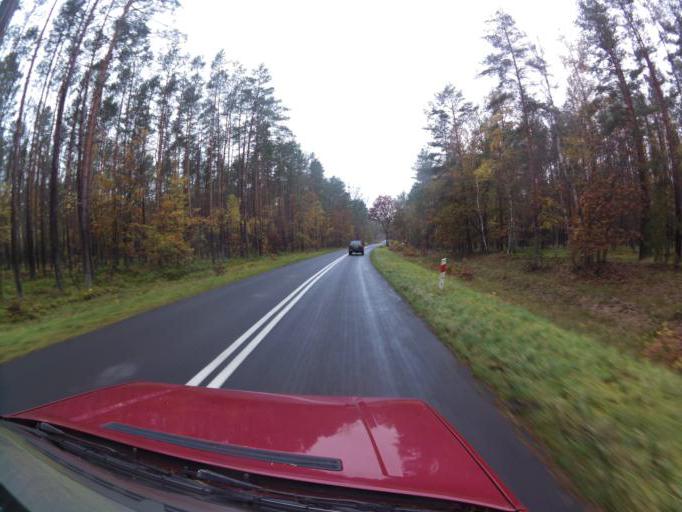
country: PL
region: West Pomeranian Voivodeship
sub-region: Powiat policki
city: Dobra
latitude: 53.5829
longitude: 14.4036
